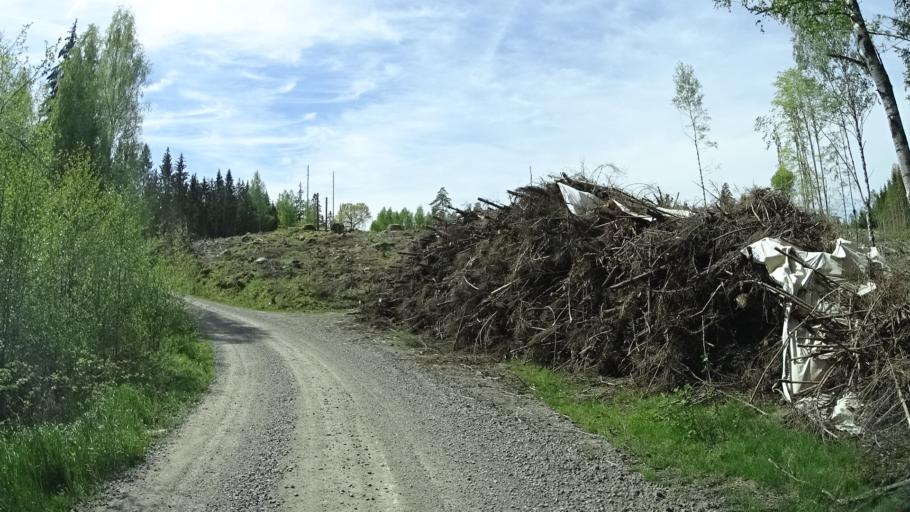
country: SE
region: OEstergoetland
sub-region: Finspangs Kommun
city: Finspang
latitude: 58.7859
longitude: 15.8467
